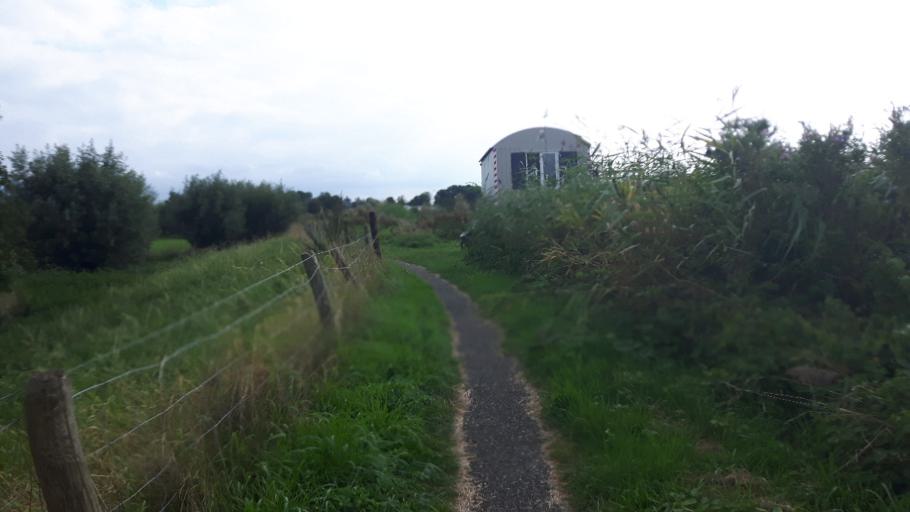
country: NL
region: North Holland
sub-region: Gemeente Ouder-Amstel
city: Ouderkerk aan de Amstel
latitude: 52.2791
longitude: 4.9264
